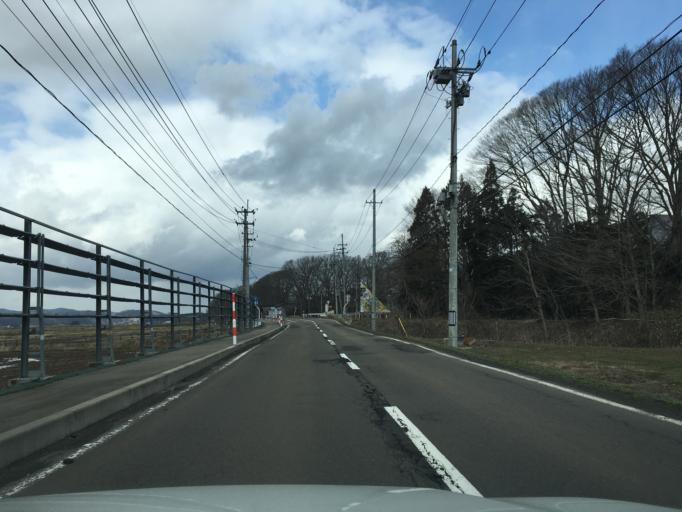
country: JP
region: Akita
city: Takanosu
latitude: 40.1423
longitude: 140.3487
